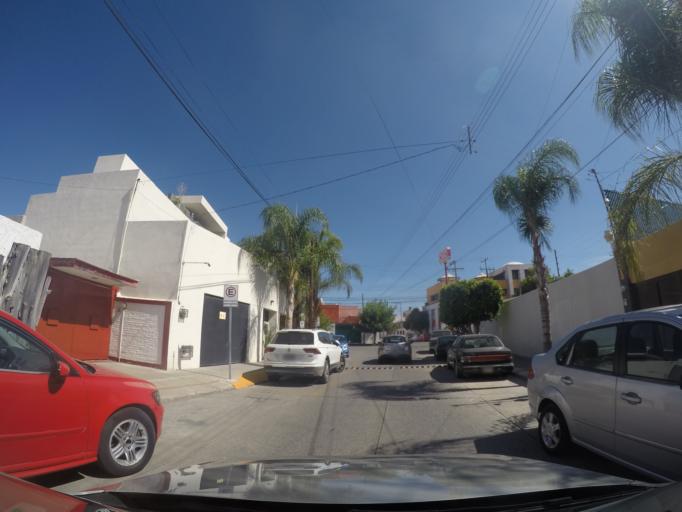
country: MX
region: San Luis Potosi
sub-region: San Luis Potosi
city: San Luis Potosi
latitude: 22.1510
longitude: -101.0094
